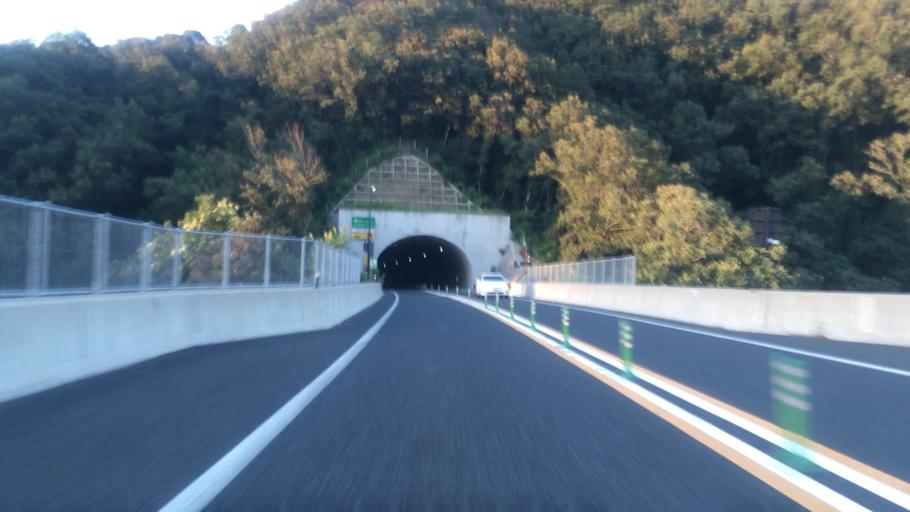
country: JP
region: Tottori
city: Tottori
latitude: 35.5544
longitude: 134.2803
